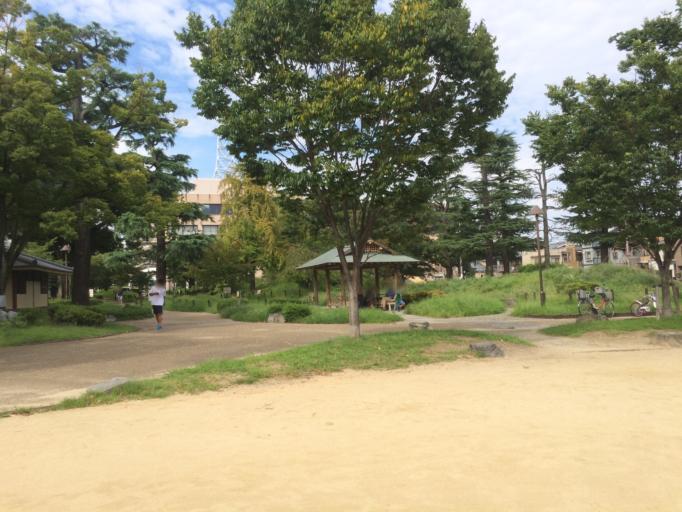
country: JP
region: Kyoto
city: Kyoto
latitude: 35.0163
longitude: 135.7458
